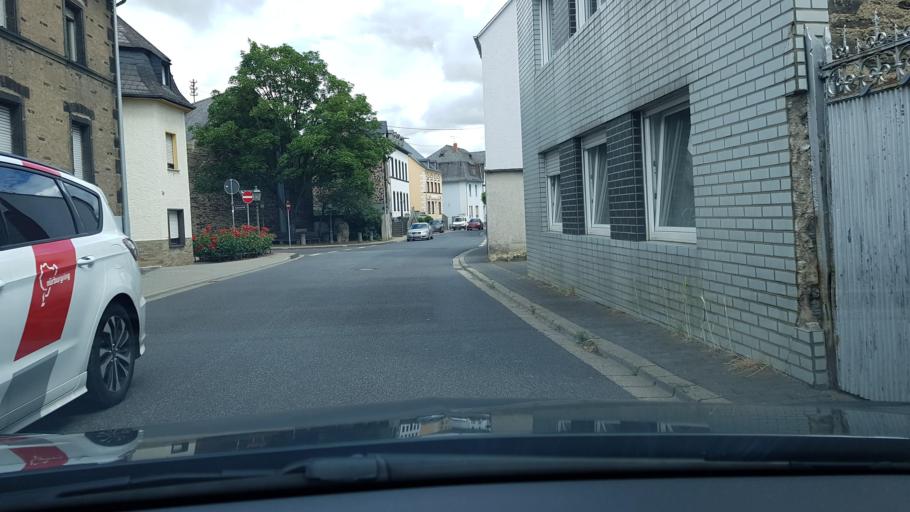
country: DE
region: Rheinland-Pfalz
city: Polch
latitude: 50.2971
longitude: 7.3123
